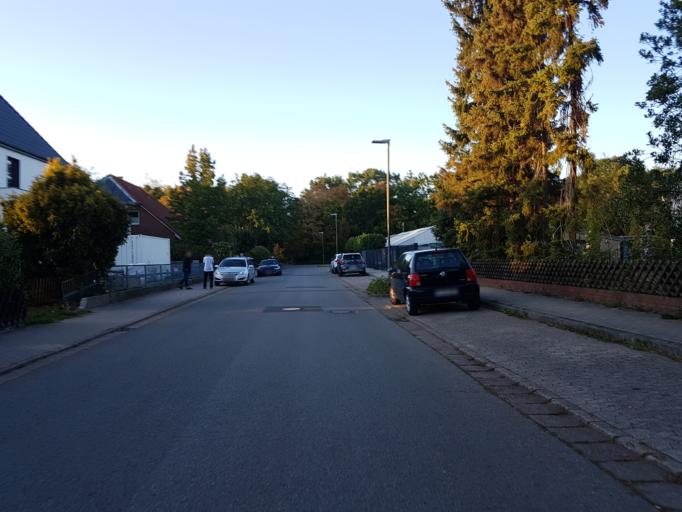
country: DE
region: Lower Saxony
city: Langenhagen
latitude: 52.4445
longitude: 9.7341
